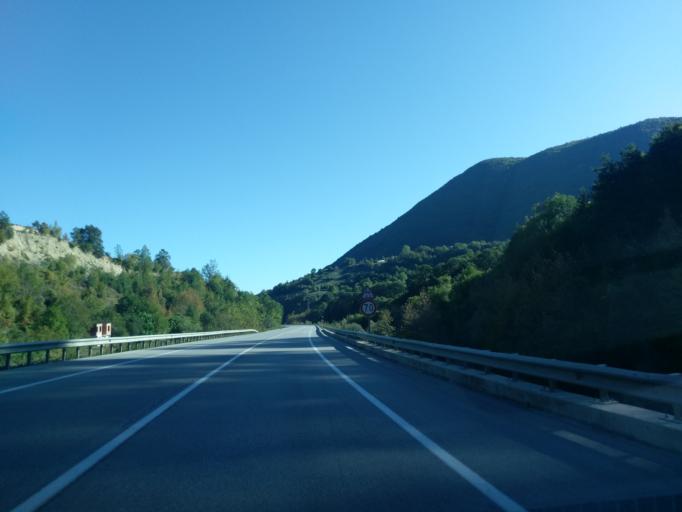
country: TR
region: Sinop
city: Kabali
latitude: 41.7824
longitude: 34.9907
